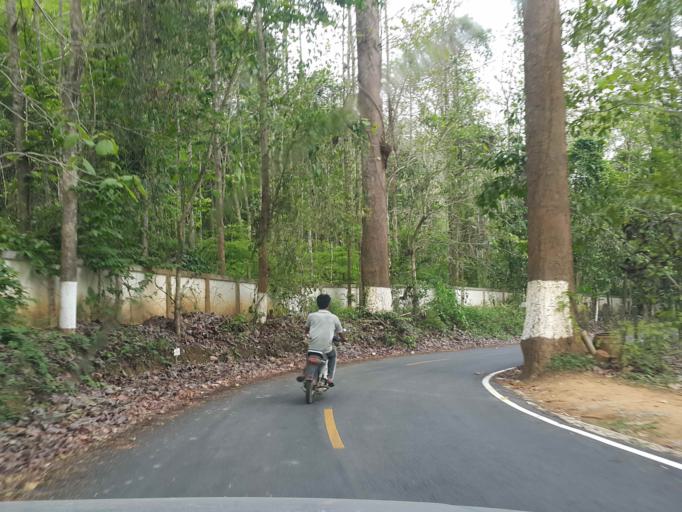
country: TH
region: Chiang Mai
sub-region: Amphoe Chiang Dao
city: Chiang Dao
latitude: 19.4048
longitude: 98.9277
